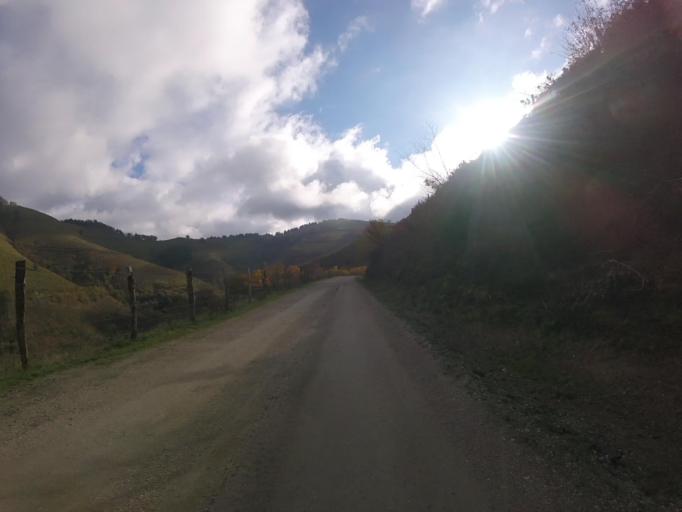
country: ES
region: Navarre
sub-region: Provincia de Navarra
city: Goizueta
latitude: 43.2086
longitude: -1.8345
